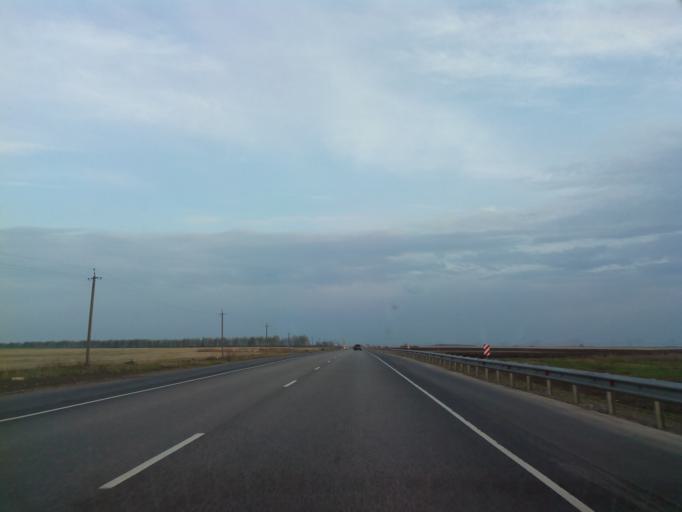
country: RU
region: Rjazan
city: Ryazhsk
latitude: 53.5869
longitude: 40.0395
